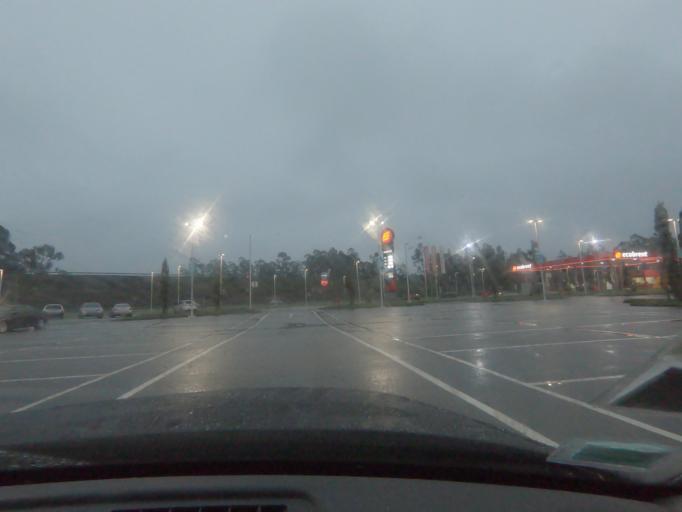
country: PT
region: Porto
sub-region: Matosinhos
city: Lavra
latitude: 41.2982
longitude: -8.7065
